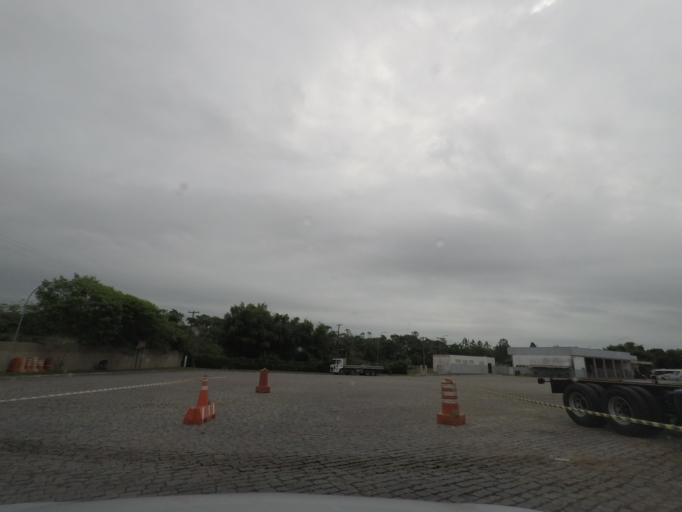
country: BR
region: Sao Paulo
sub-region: Registro
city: Registro
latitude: -24.5308
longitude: -47.8578
